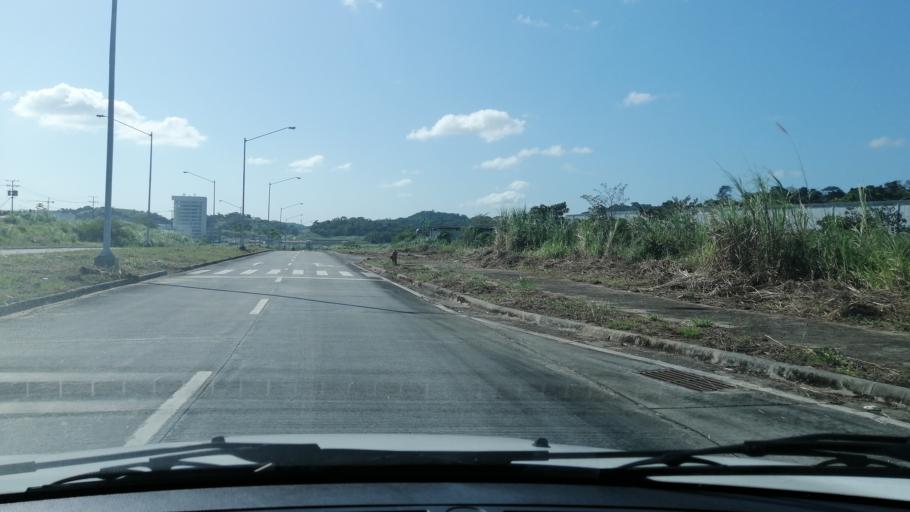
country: PA
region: Panama
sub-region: Distrito de Panama
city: Paraiso
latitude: 9.0294
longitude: -79.5815
